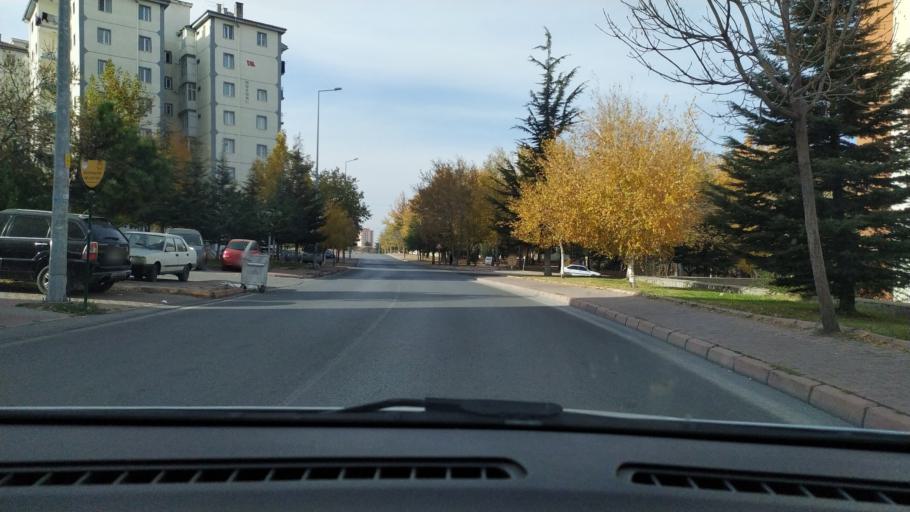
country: TR
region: Kayseri
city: Melikgazi
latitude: 38.7369
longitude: 35.3905
